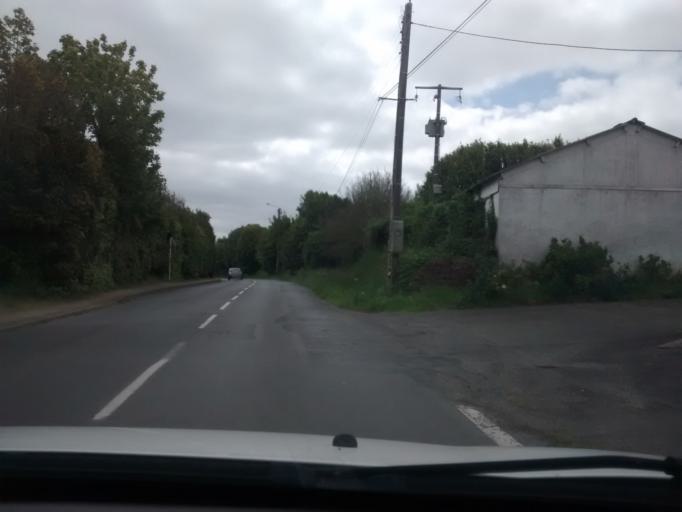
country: FR
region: Brittany
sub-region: Departement des Cotes-d'Armor
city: Perros-Guirec
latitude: 48.8062
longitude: -3.4589
